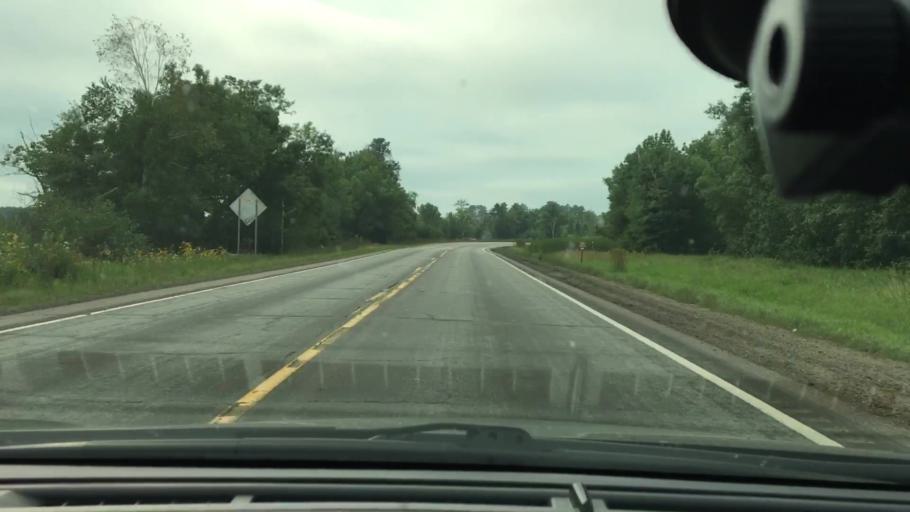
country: US
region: Minnesota
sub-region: Crow Wing County
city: Cross Lake
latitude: 46.7194
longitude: -93.9552
